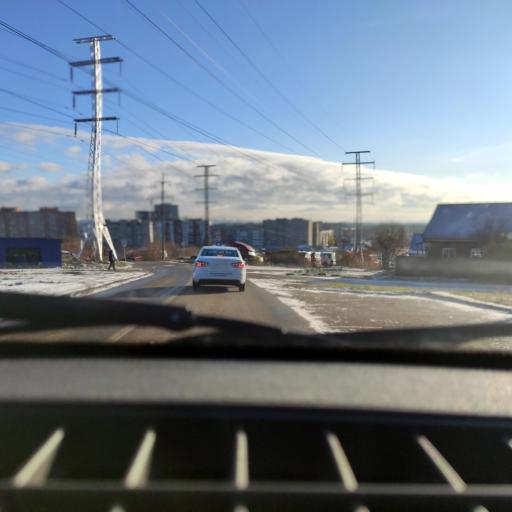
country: RU
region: Bashkortostan
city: Avdon
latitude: 54.6948
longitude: 55.8096
